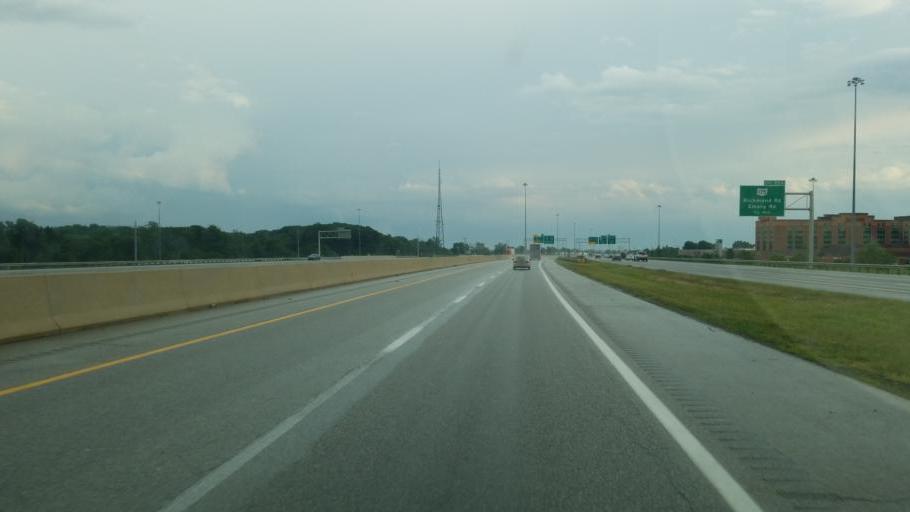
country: US
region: Ohio
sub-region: Cuyahoga County
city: Orange
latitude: 41.4521
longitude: -81.4913
